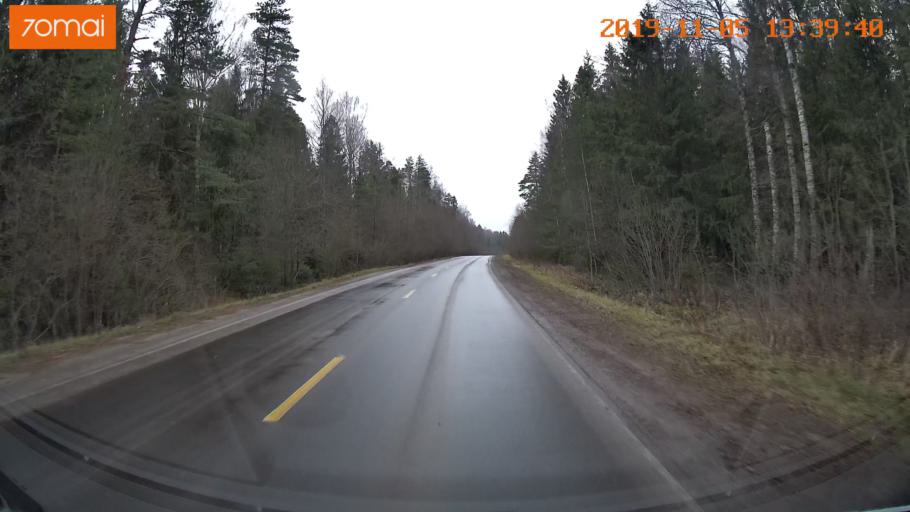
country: RU
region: Ivanovo
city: Shuya
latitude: 56.9419
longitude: 41.3854
